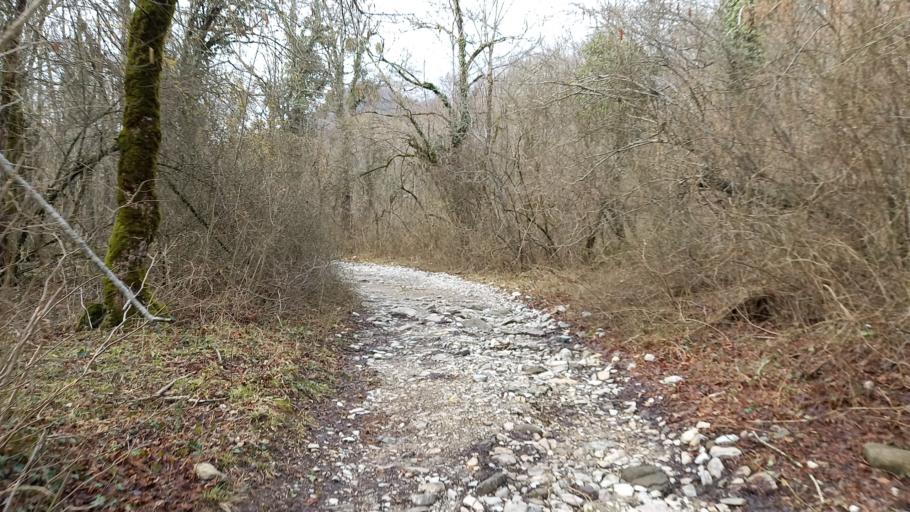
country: RU
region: Krasnodarskiy
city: Dzhubga
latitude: 44.4128
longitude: 38.7196
